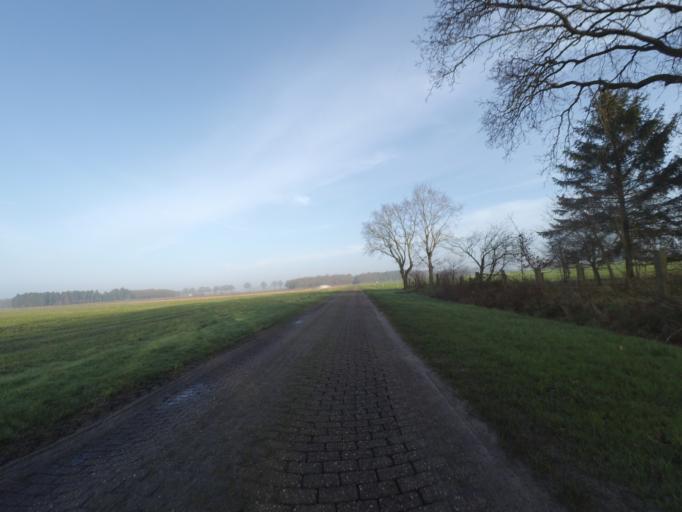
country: NL
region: Drenthe
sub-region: Gemeente Borger-Odoorn
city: Borger
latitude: 52.8947
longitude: 6.8014
